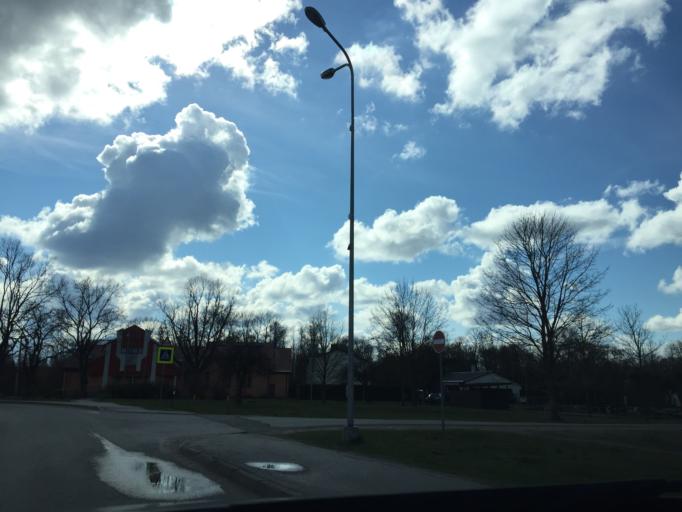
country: LV
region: Kekava
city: Kekava
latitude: 56.8271
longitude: 24.2369
